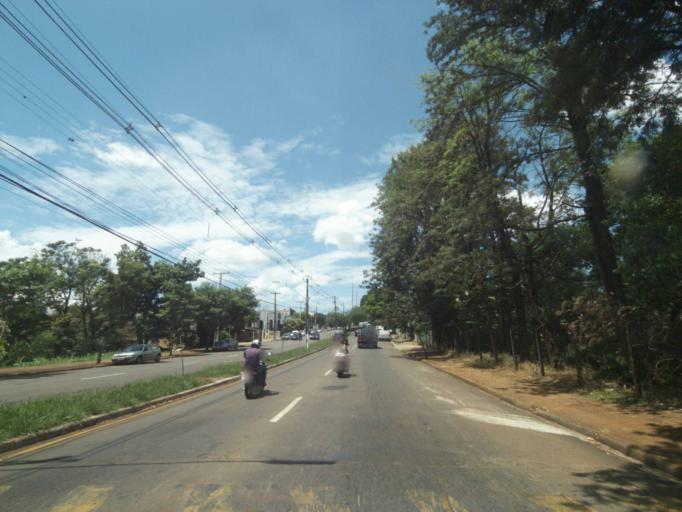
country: BR
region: Parana
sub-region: Londrina
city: Londrina
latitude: -23.3120
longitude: -51.2059
